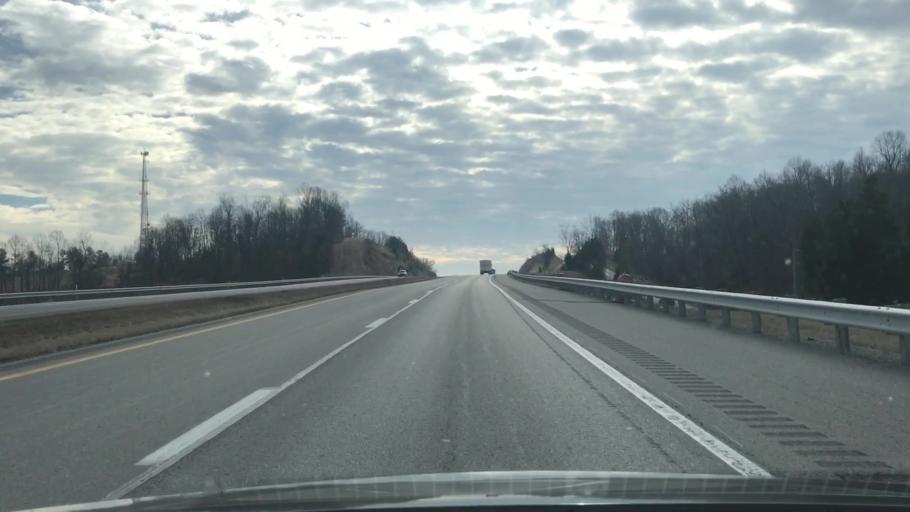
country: US
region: Kentucky
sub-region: Ohio County
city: Hartford
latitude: 37.5297
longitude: -86.9221
